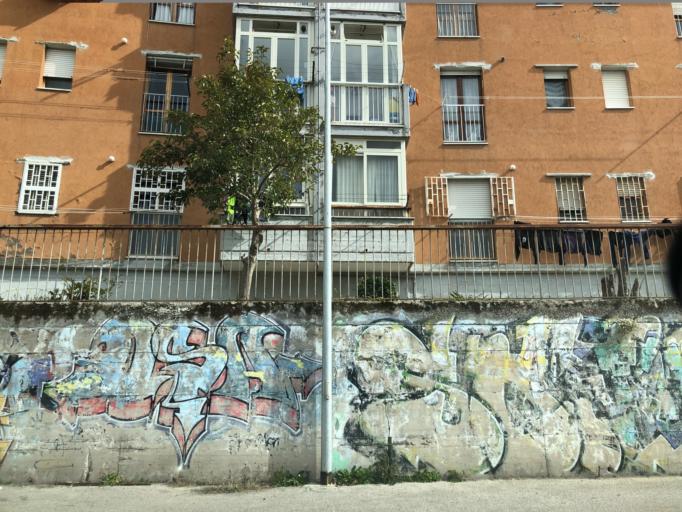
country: IT
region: Campania
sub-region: Provincia di Napoli
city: San Sebastiano al Vesuvio
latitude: 40.8413
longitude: 14.3619
